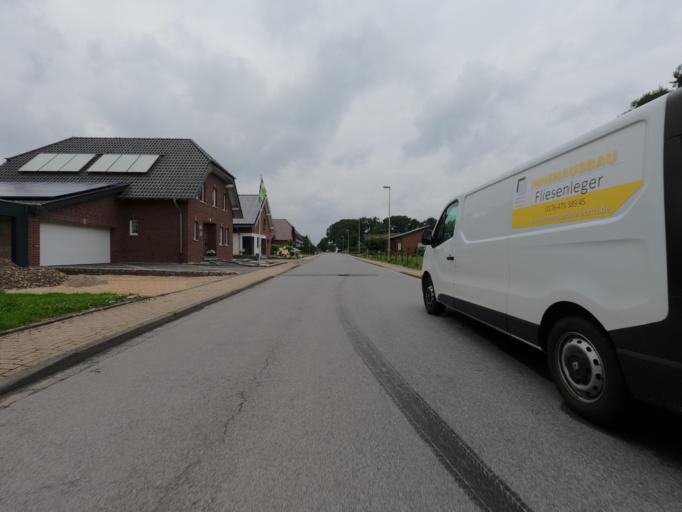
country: DE
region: North Rhine-Westphalia
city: Geilenkirchen
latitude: 50.9645
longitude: 6.1698
